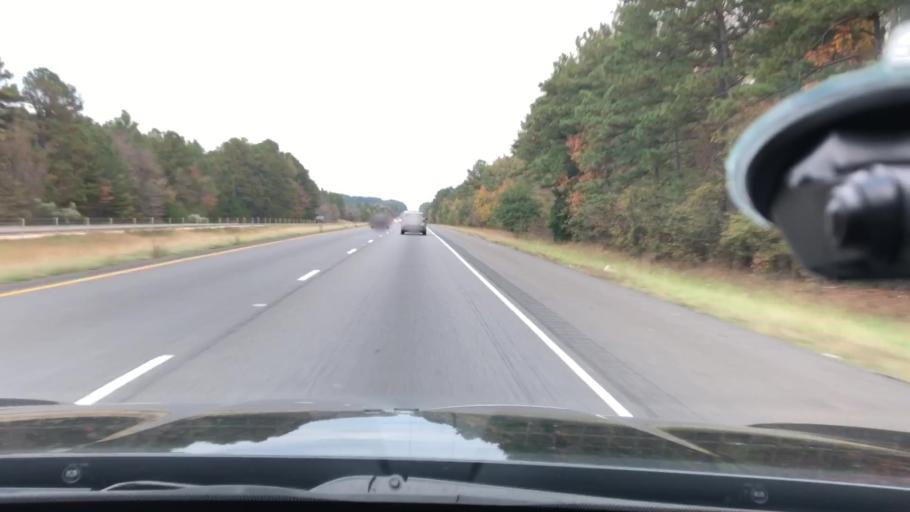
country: US
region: Arkansas
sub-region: Clark County
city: Arkadelphia
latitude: 34.2555
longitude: -92.9865
